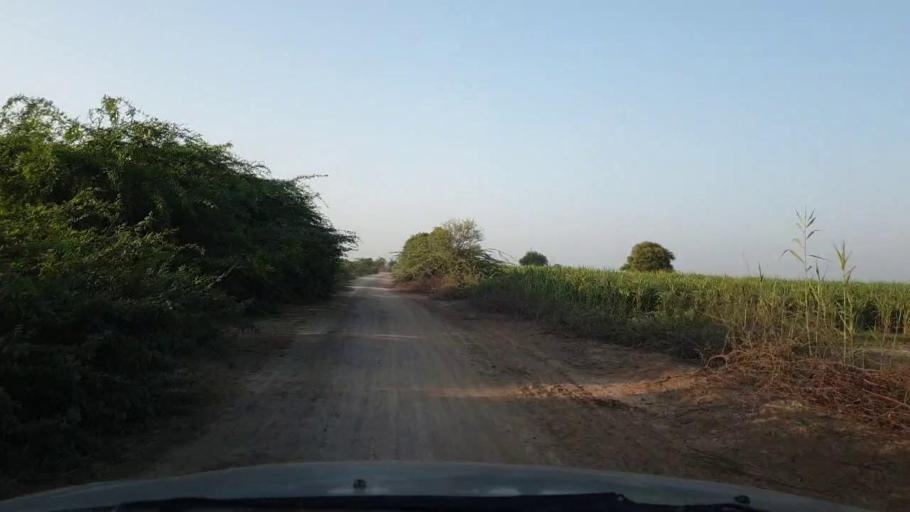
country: PK
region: Sindh
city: Tando Ghulam Ali
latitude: 25.1089
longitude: 68.9487
